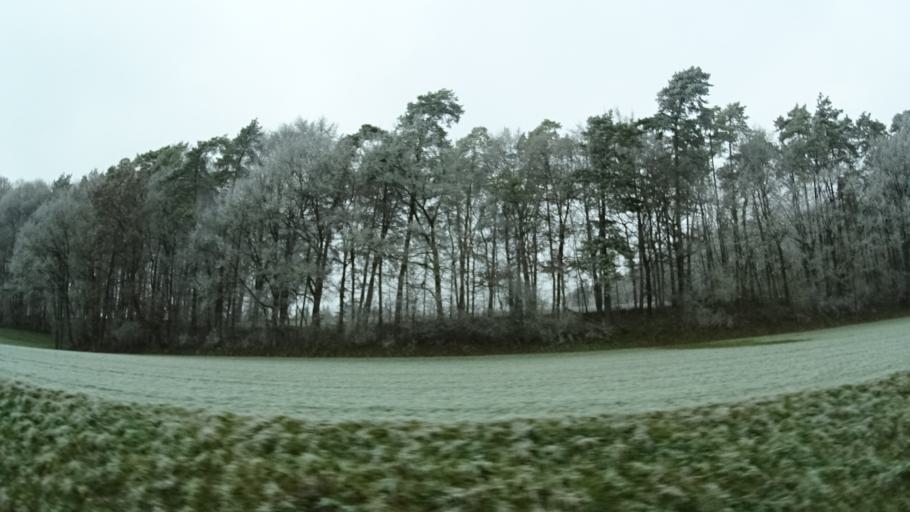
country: DE
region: Baden-Wuerttemberg
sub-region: Regierungsbezirk Stuttgart
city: Igersheim
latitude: 49.5458
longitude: 9.8201
